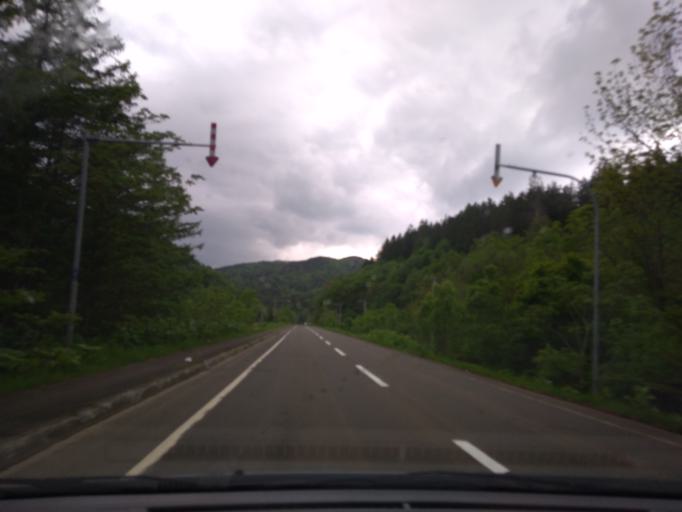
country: JP
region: Hokkaido
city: Shimo-furano
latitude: 43.1248
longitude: 142.4067
